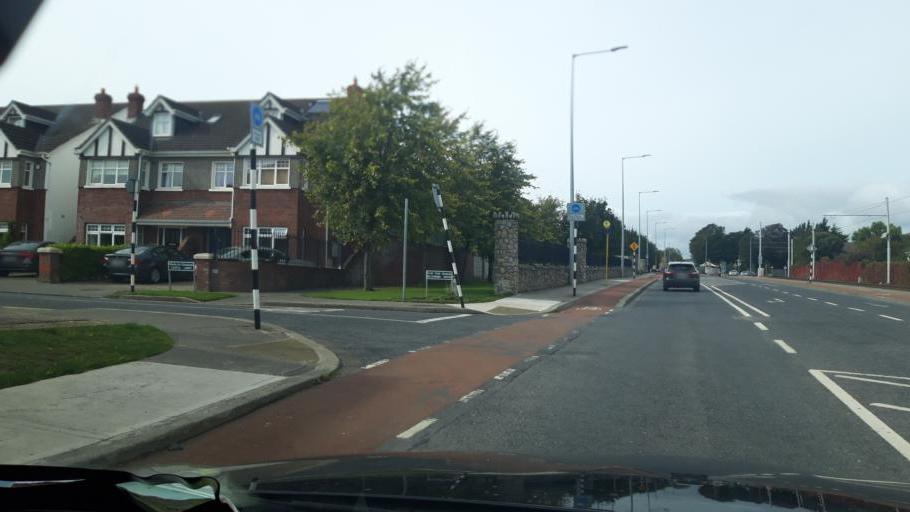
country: IE
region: Leinster
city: Sandyford
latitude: 53.2616
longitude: -6.2079
